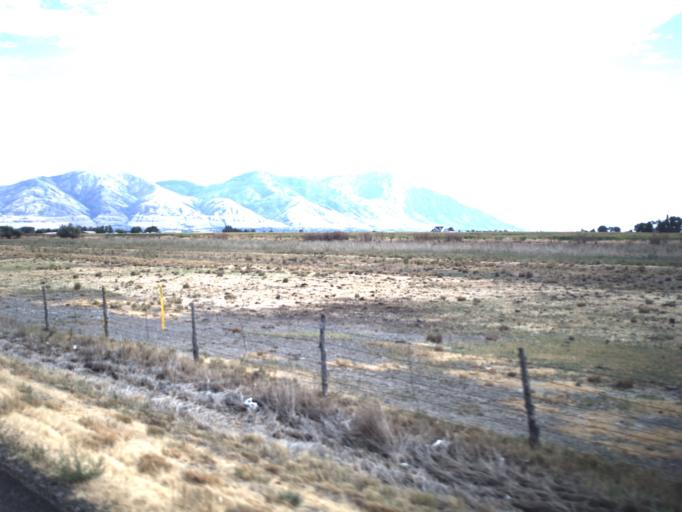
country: US
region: Utah
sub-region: Box Elder County
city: Honeyville
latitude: 41.5577
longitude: -112.1411
